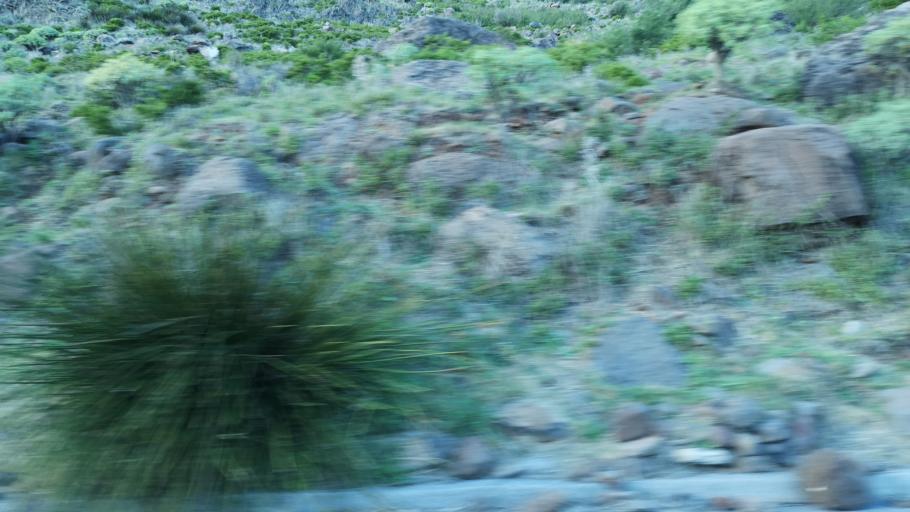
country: ES
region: Canary Islands
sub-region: Provincia de Santa Cruz de Tenerife
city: Alajero
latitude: 28.0892
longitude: -17.2530
